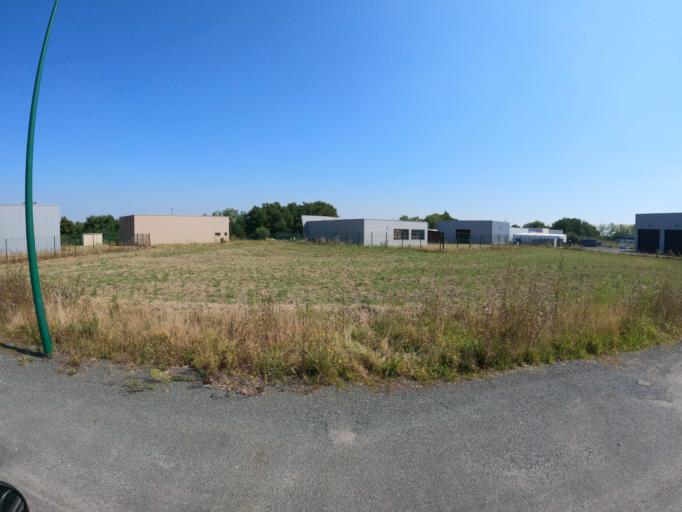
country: FR
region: Pays de la Loire
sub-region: Departement de la Loire-Atlantique
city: Geneston
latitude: 47.0657
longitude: -1.5043
